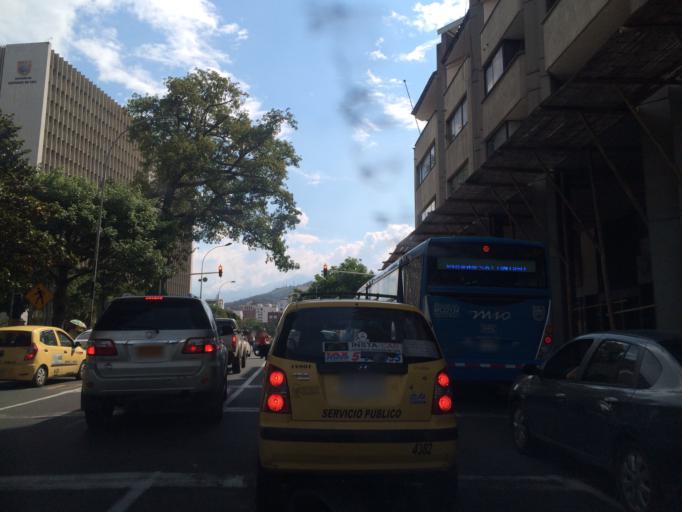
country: CO
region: Valle del Cauca
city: Cali
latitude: 3.4557
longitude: -76.5333
